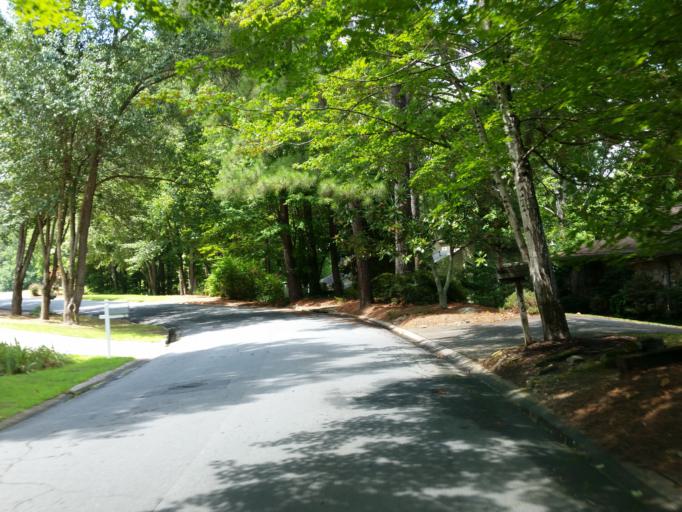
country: US
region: Georgia
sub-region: Fulton County
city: Roswell
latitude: 34.0441
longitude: -84.4276
